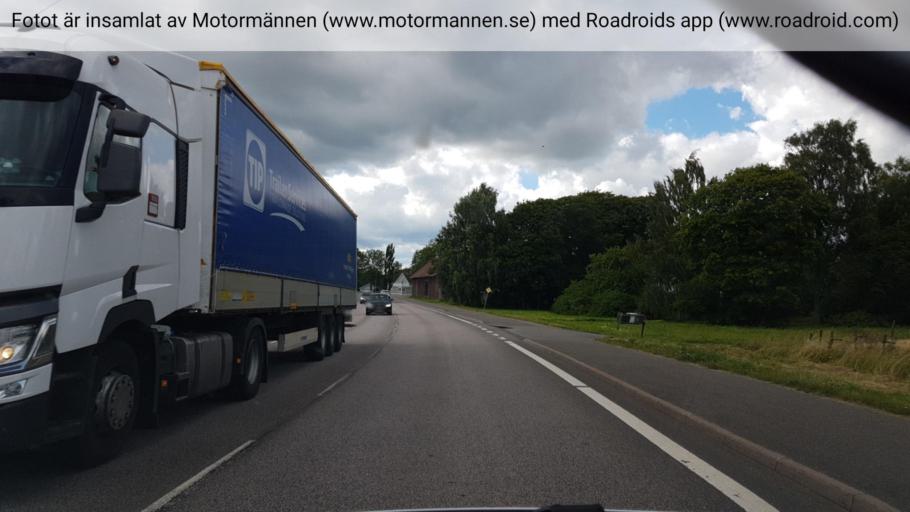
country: SE
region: Vaestra Goetaland
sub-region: Falkopings Kommun
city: Falkoeping
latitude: 58.0256
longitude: 13.5571
